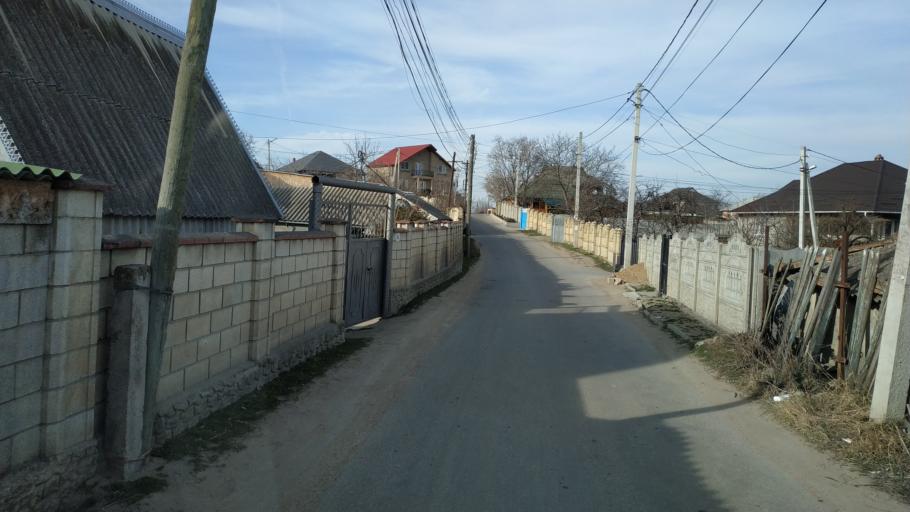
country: MD
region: Chisinau
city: Vatra
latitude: 47.0728
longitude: 28.6720
